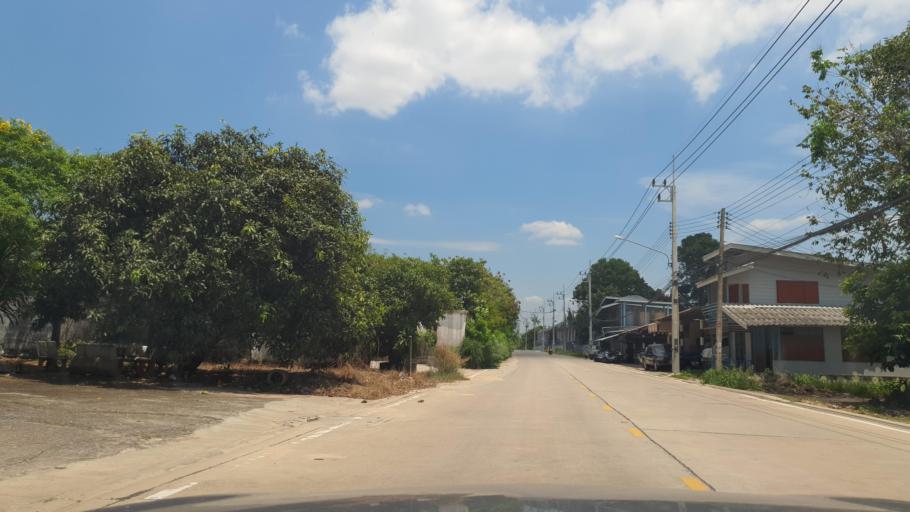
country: TH
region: Chon Buri
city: Phatthaya
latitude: 12.8152
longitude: 100.9353
